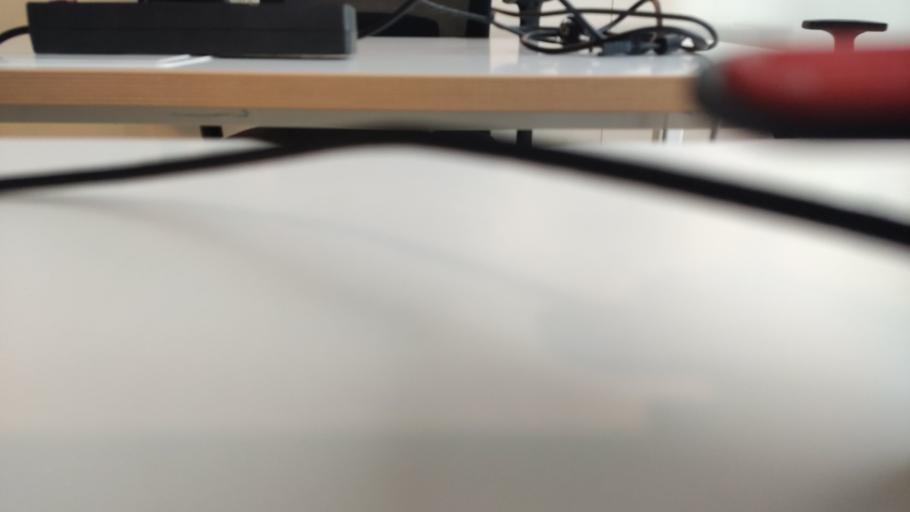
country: RU
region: Moskovskaya
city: Rogachevo
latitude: 56.4115
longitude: 37.0519
